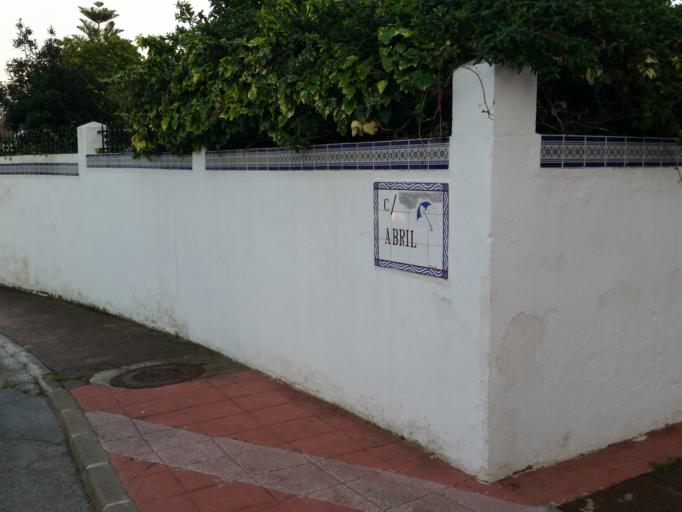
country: ES
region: Andalusia
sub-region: Provincia de Malaga
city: Torremolinos
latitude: 36.6041
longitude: -4.5257
